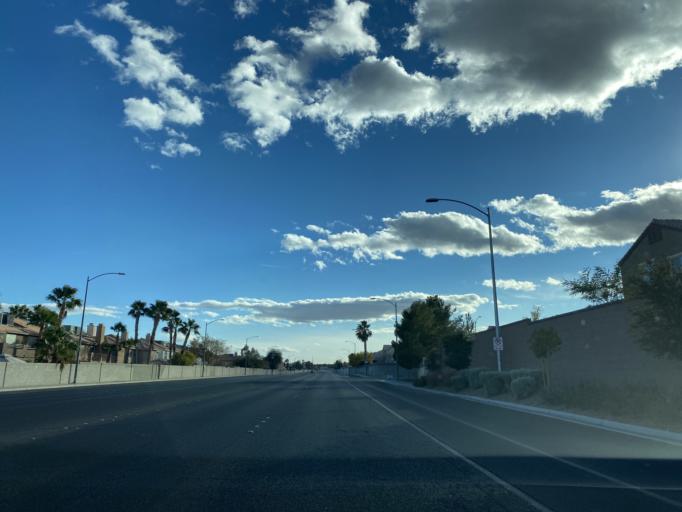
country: US
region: Nevada
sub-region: Clark County
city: Summerlin South
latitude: 36.2286
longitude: -115.2975
